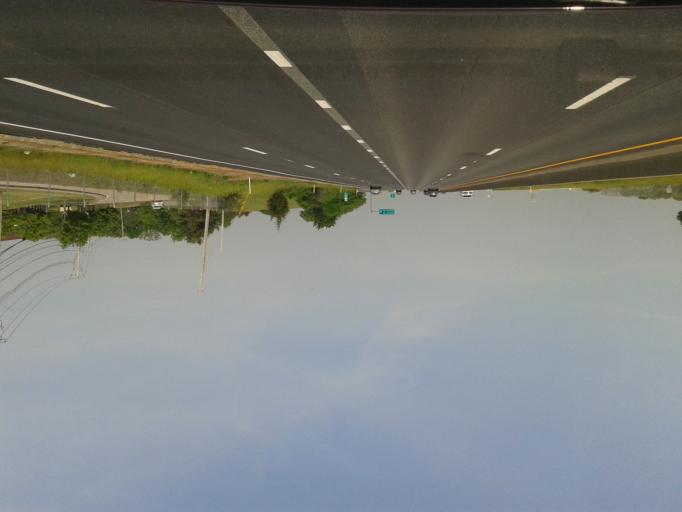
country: US
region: Massachusetts
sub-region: Worcester County
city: Westborough
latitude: 42.2887
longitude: -71.5786
